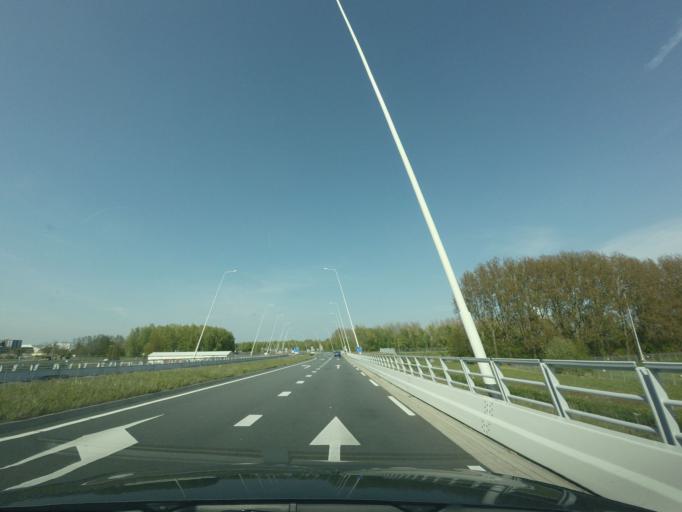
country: NL
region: North Holland
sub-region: Gemeente Amsterdam
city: Driemond
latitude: 52.3395
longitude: 5.0130
